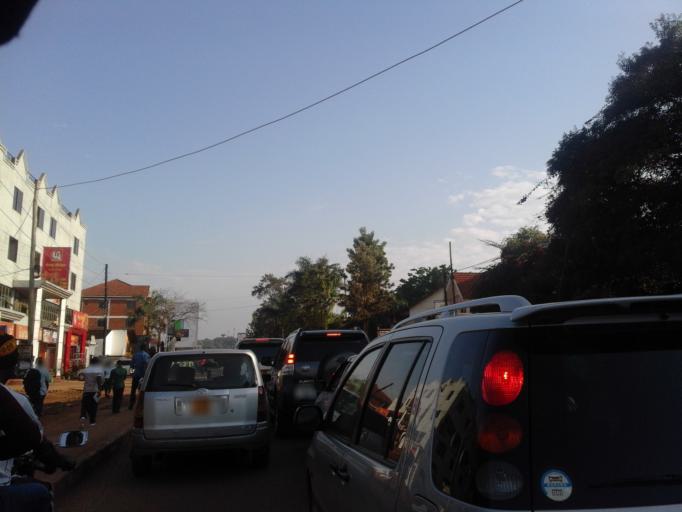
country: UG
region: Central Region
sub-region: Kampala District
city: Kampala
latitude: 0.2919
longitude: 32.6057
